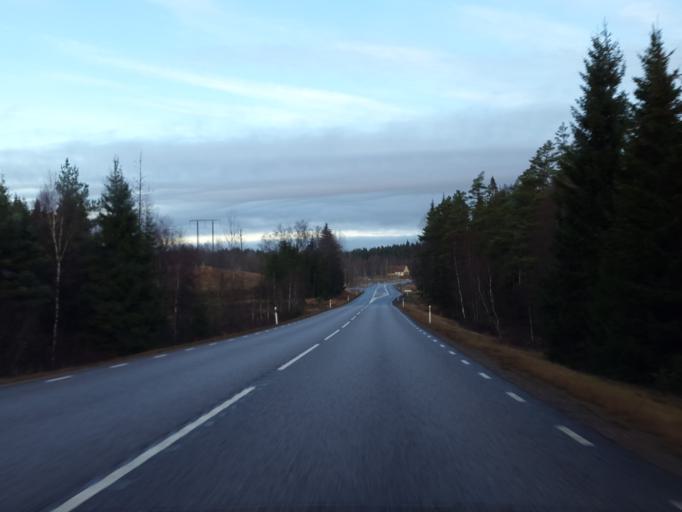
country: SE
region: Vaestra Goetaland
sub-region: Boras Kommun
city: Sandared
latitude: 57.7769
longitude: 12.7865
